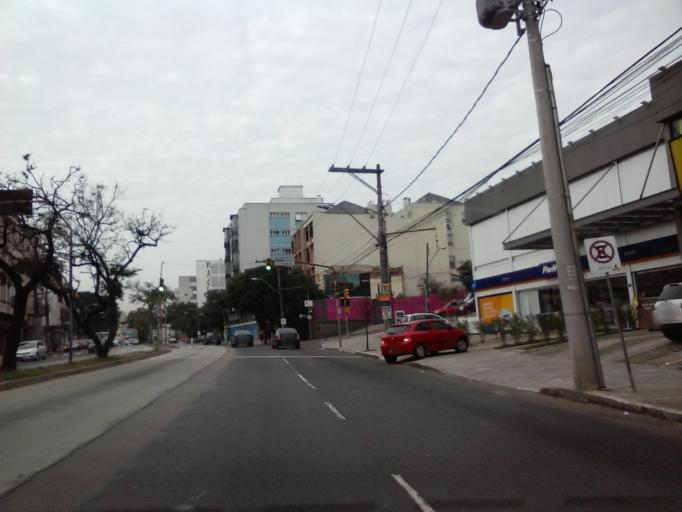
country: BR
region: Rio Grande do Sul
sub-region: Porto Alegre
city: Porto Alegre
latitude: -30.0435
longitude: -51.1880
